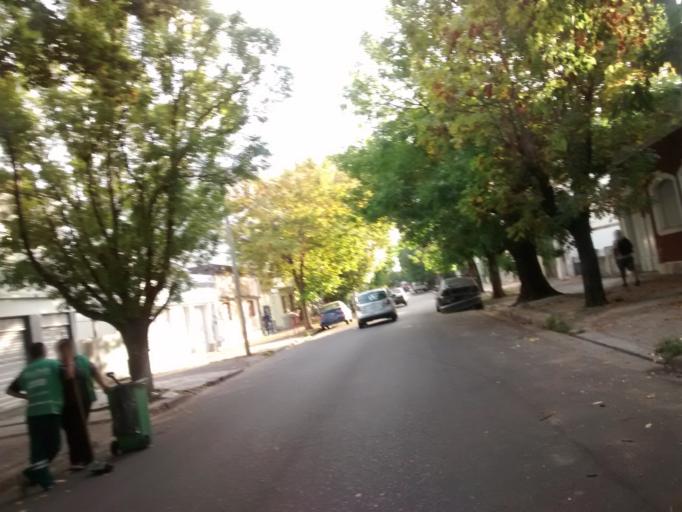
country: AR
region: Buenos Aires
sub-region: Partido de La Plata
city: La Plata
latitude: -34.9245
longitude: -57.9269
